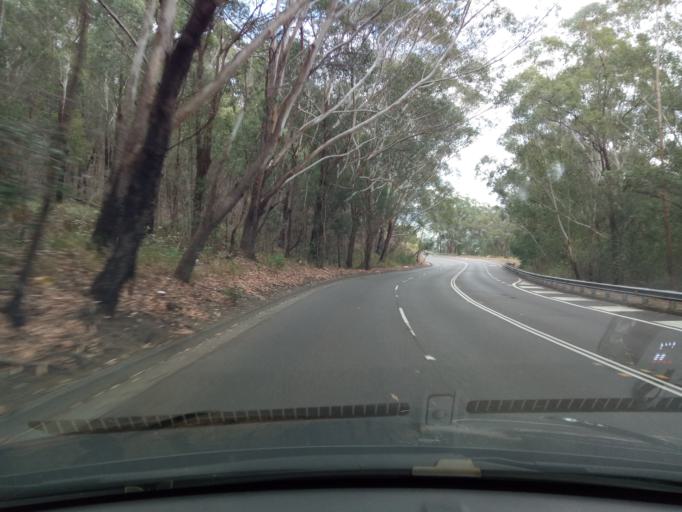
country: AU
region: New South Wales
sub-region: Gosford Shire
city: Gosford
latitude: -33.4220
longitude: 151.3466
